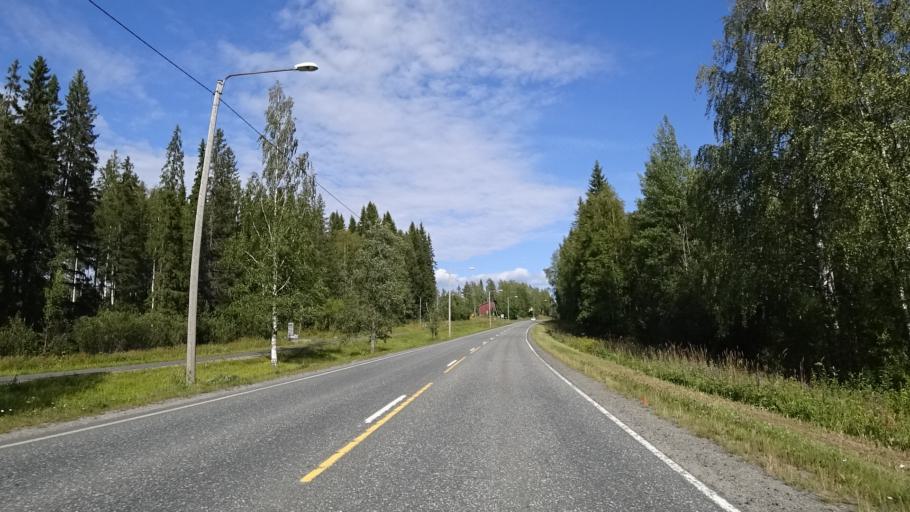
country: FI
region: North Karelia
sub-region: Joensuu
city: Eno
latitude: 62.8046
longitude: 30.1262
